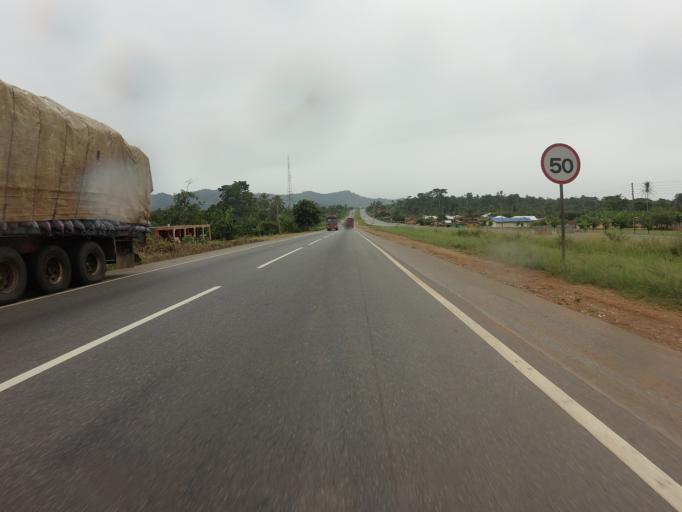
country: GH
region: Eastern
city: Suhum
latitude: 6.0993
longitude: -0.4831
